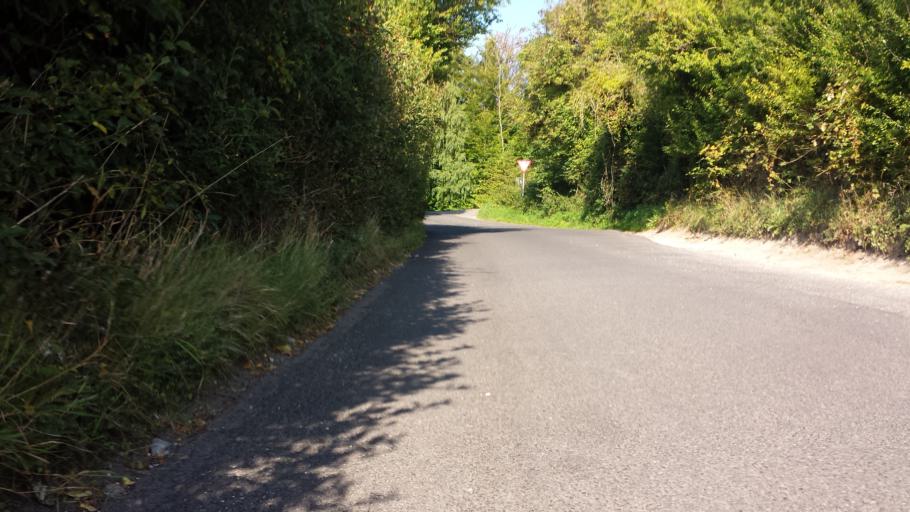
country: GB
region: England
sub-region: Kent
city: Eynsford
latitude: 51.3569
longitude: 0.2003
